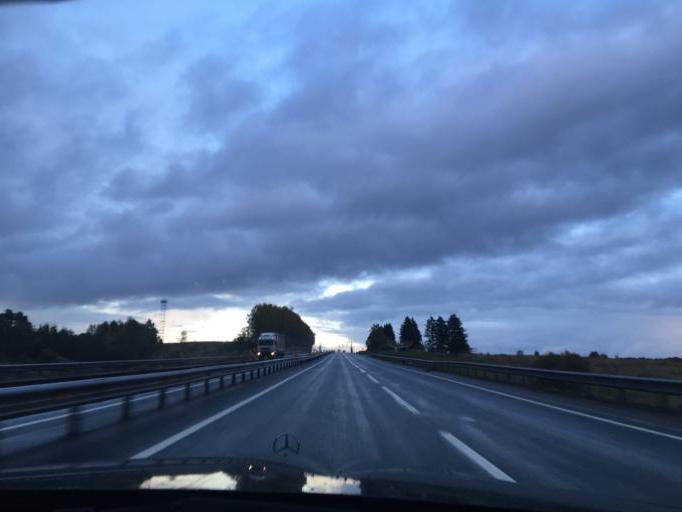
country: RU
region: Smolensk
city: Yartsevo
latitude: 55.0629
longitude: 32.6091
